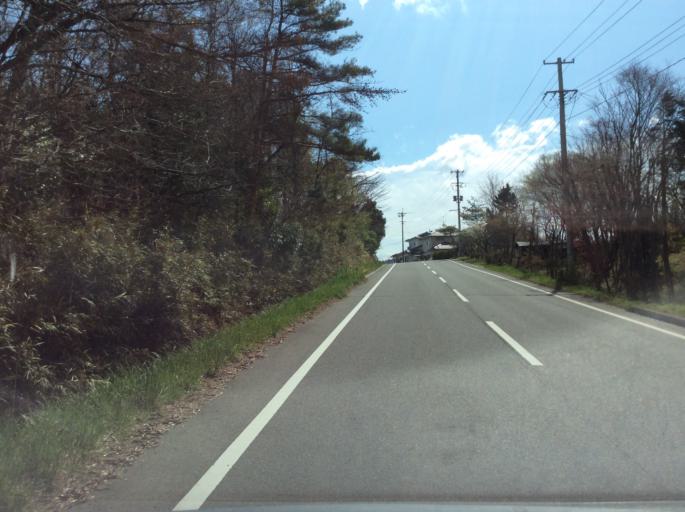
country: JP
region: Fukushima
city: Koriyama
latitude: 37.3543
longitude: 140.4102
